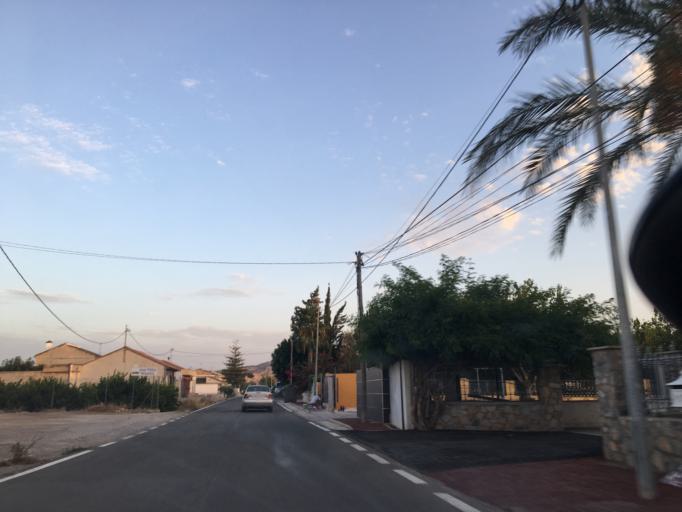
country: ES
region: Murcia
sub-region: Murcia
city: Santomera
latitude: 38.0298
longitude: -1.0590
